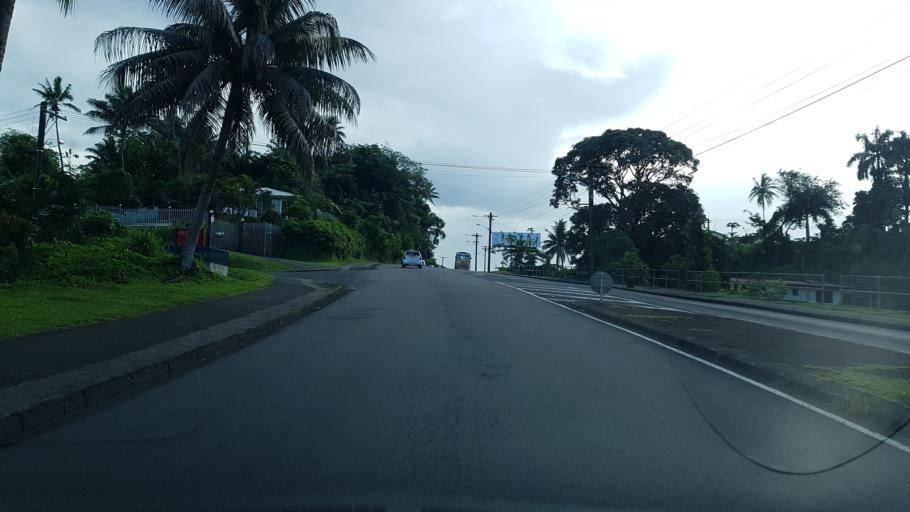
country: FJ
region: Central
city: Suva
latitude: -18.1459
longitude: 178.4391
